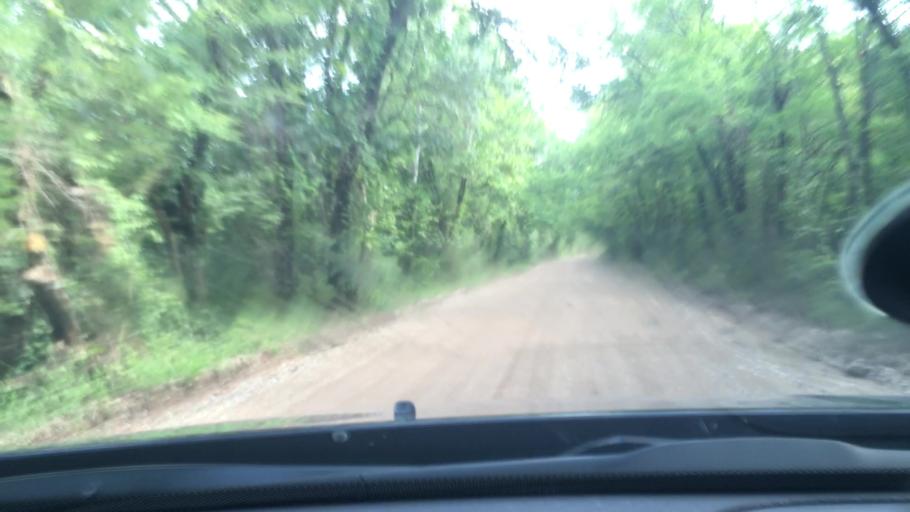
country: US
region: Oklahoma
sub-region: Atoka County
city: Atoka
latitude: 34.4495
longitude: -96.0673
